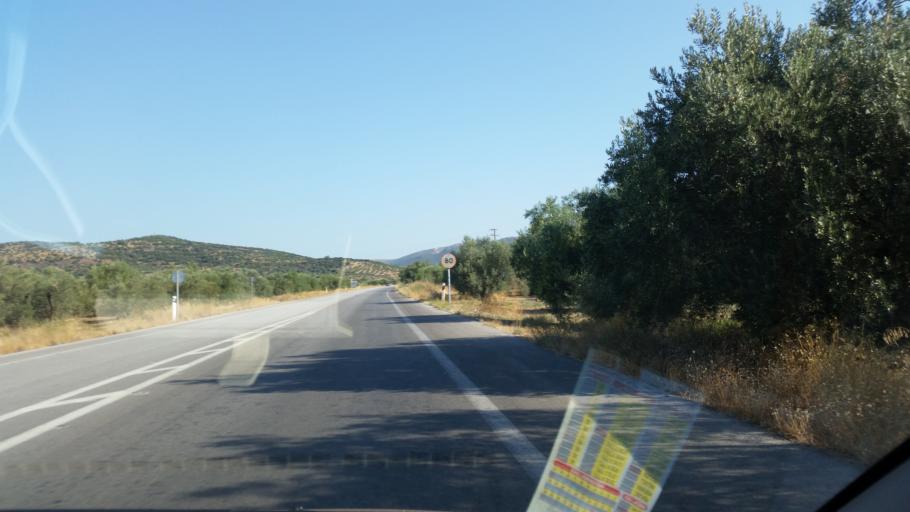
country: GR
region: Peloponnese
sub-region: Nomos Argolidos
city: Koutsopodi
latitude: 37.7209
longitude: 22.7352
